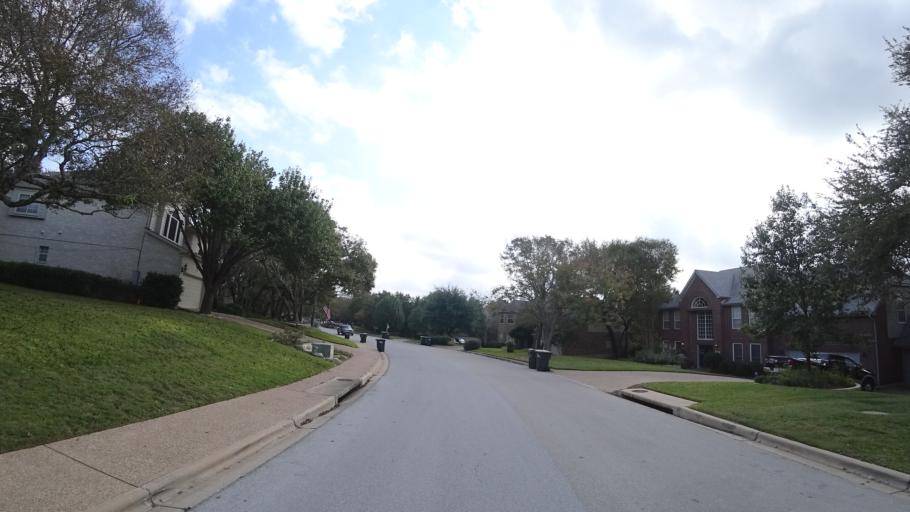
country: US
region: Texas
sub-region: Travis County
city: Barton Creek
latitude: 30.3002
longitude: -97.8859
